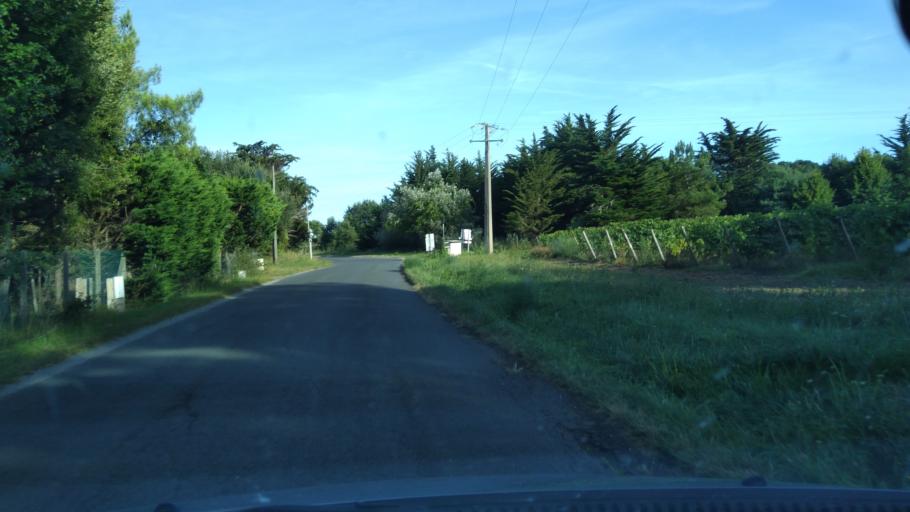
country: FR
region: Poitou-Charentes
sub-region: Departement de la Charente-Maritime
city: Saint-Denis-d'Oleron
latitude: 45.9556
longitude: -1.3568
